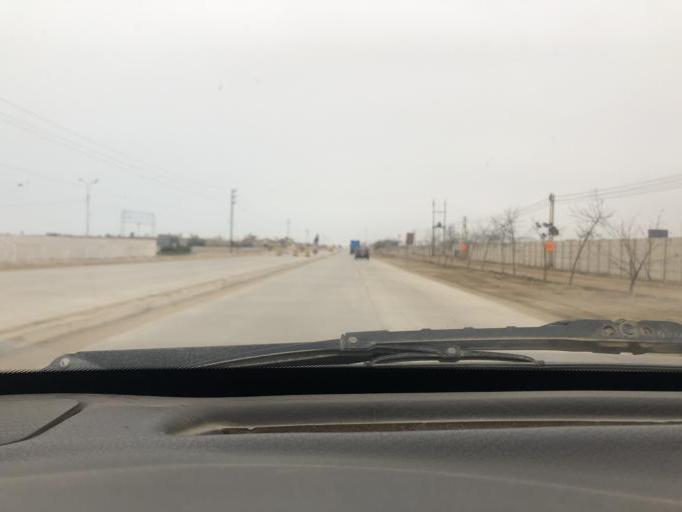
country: PE
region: Lima
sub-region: Lima
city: San Bartolo
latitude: -12.3775
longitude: -76.7816
